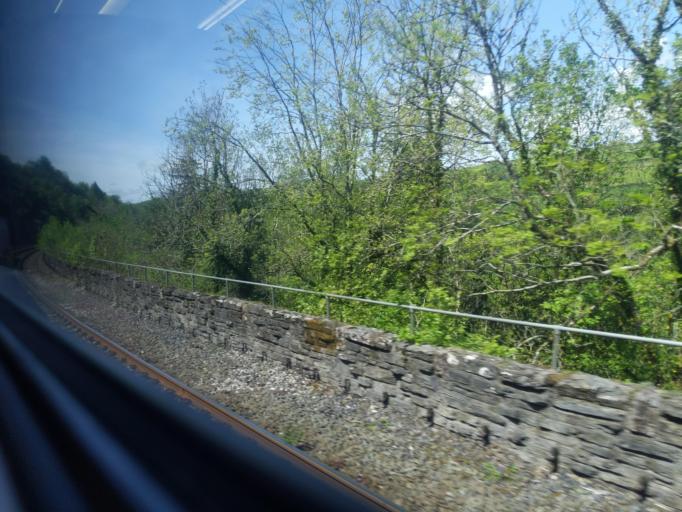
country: GB
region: England
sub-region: Cornwall
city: Lostwithiel
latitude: 50.4546
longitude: -4.5896
